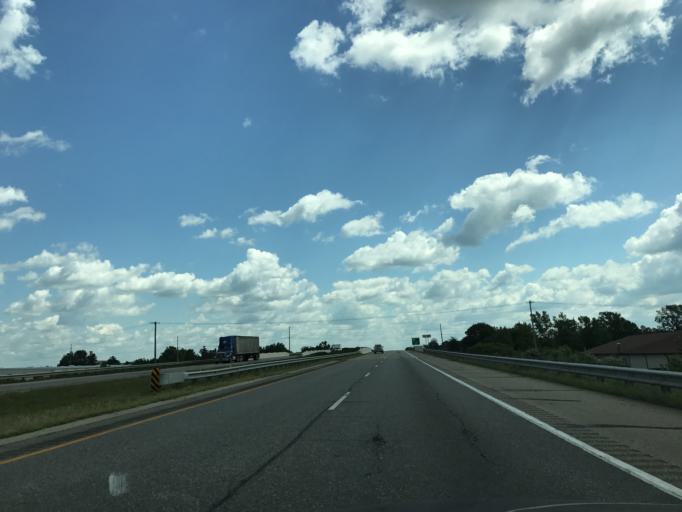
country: US
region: Indiana
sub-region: Marshall County
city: Plymouth
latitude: 41.3617
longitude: -86.3183
